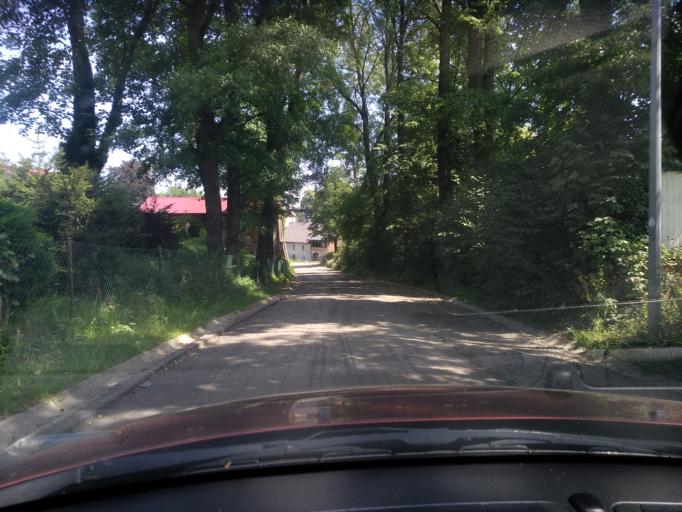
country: PL
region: Lower Silesian Voivodeship
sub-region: Powiat lwowecki
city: Mirsk
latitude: 50.9775
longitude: 15.3465
